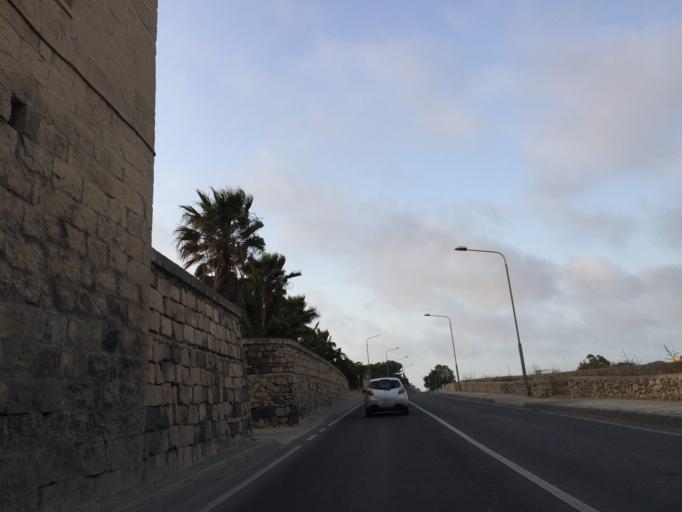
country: MT
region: Il-Mosta
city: Mosta
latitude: 35.9124
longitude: 14.4145
